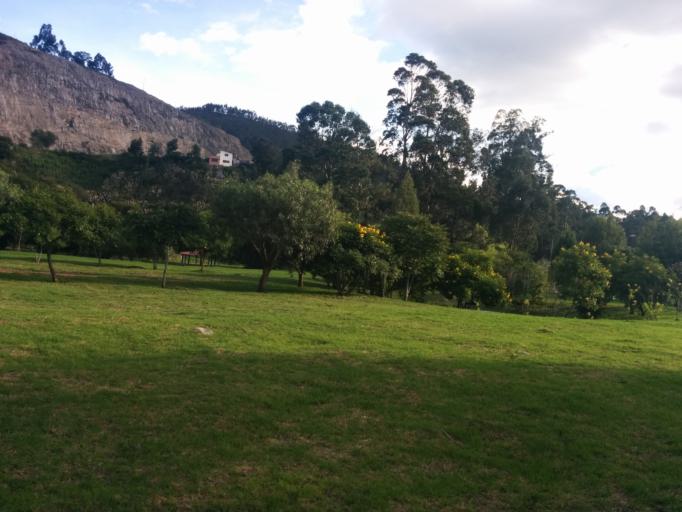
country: EC
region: Azuay
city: Cuenca
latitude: -2.8873
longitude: -78.9556
